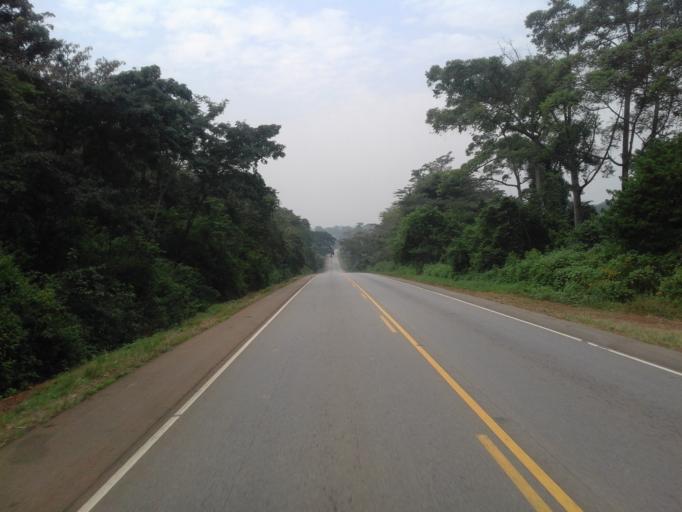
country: UG
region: Eastern Region
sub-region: Busia District
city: Busia
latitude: 0.5435
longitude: 34.0138
